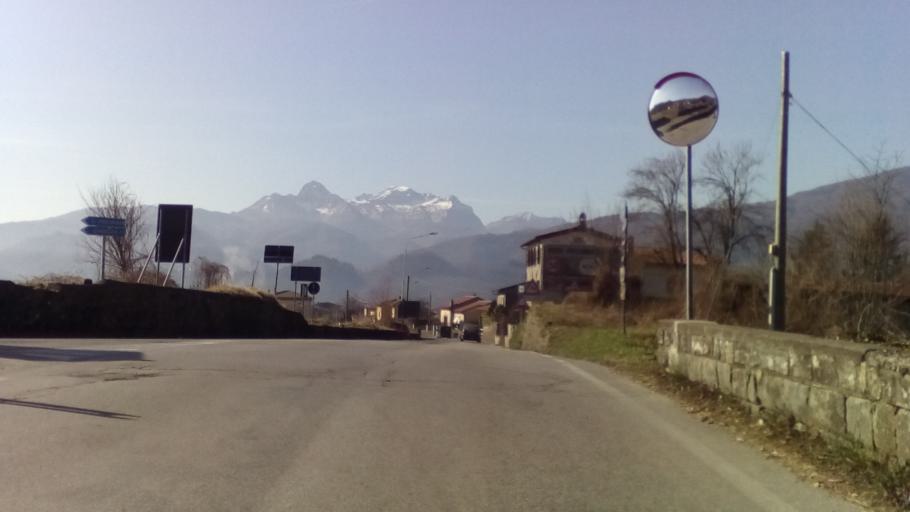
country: IT
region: Tuscany
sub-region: Provincia di Lucca
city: Pieve Fosciana
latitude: 44.1376
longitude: 10.4173
